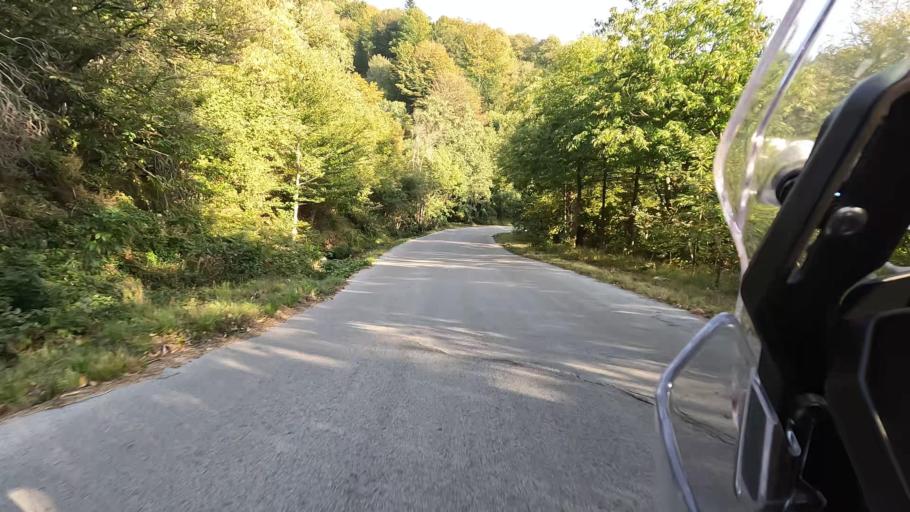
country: IT
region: Liguria
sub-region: Provincia di Savona
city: San Giovanni
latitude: 44.4191
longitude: 8.5300
